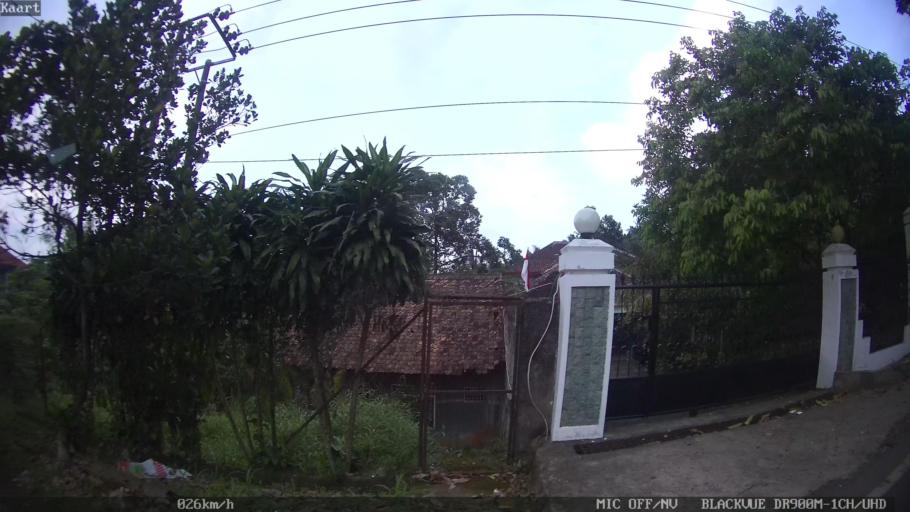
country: ID
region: Lampung
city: Bandarlampung
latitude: -5.4058
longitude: 105.2169
